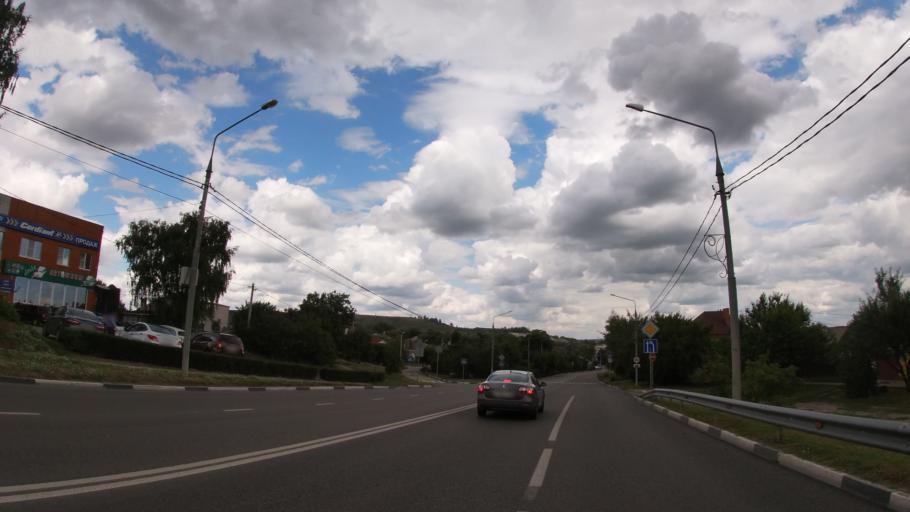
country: RU
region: Belgorod
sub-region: Belgorodskiy Rayon
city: Belgorod
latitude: 50.6052
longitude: 36.6110
